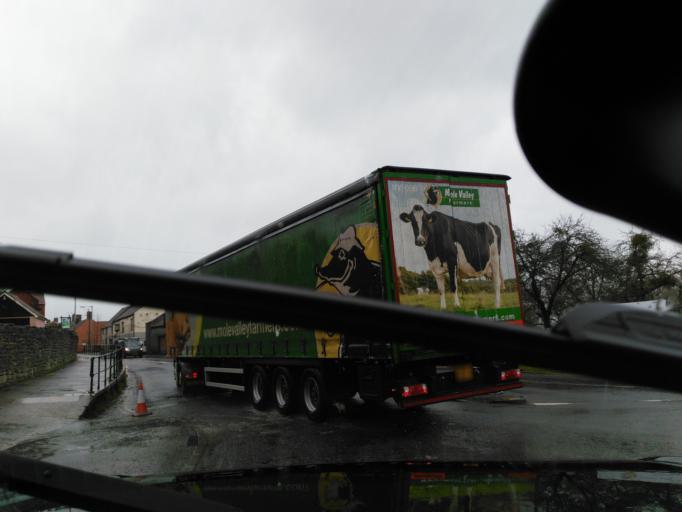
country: GB
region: England
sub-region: Somerset
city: Glastonbury
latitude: 51.1446
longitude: -2.7104
